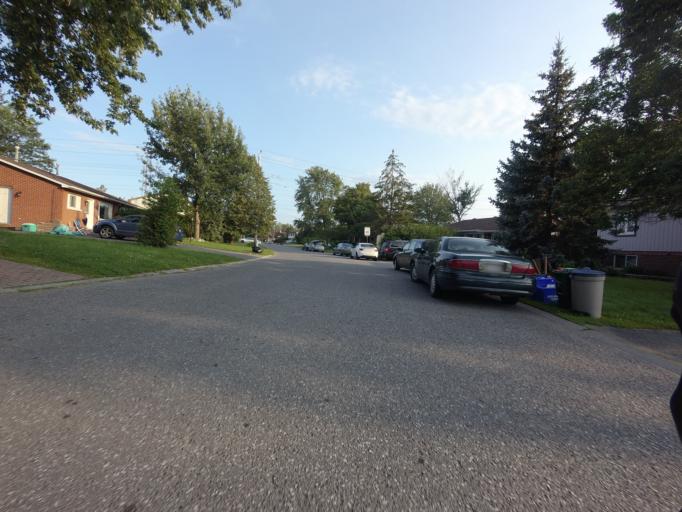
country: CA
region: Ontario
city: Bells Corners
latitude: 45.3332
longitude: -75.7471
